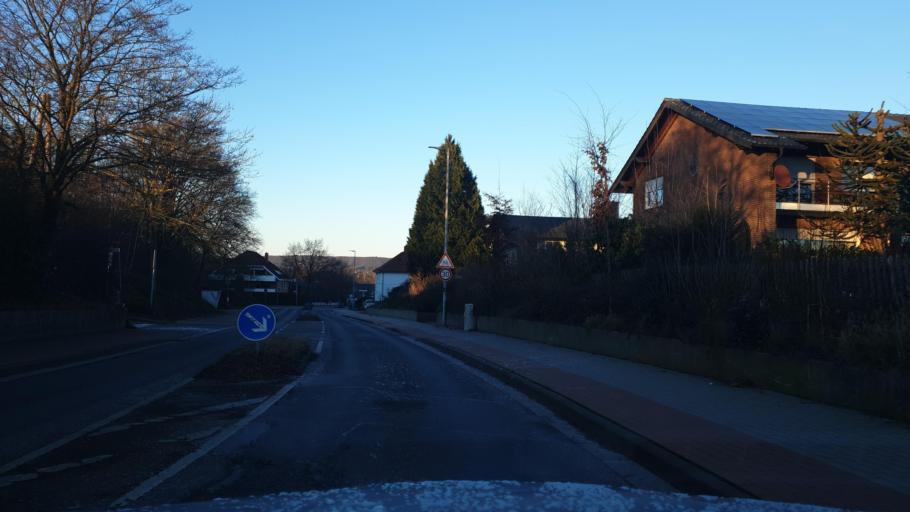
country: DE
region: North Rhine-Westphalia
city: Bad Oeynhausen
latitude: 52.2025
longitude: 8.8209
